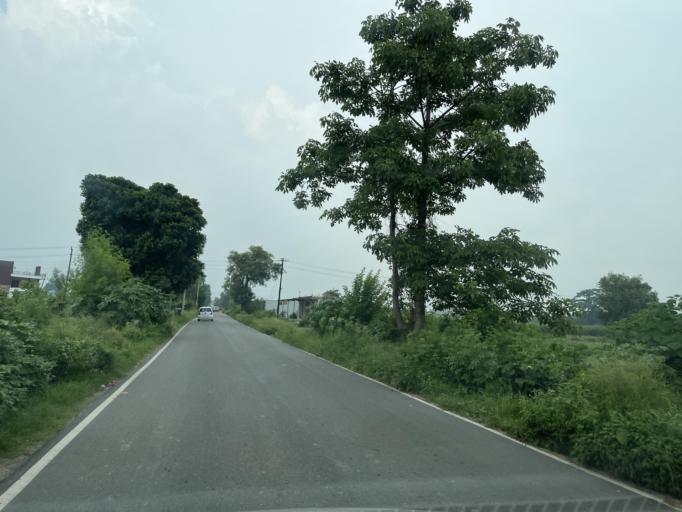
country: IN
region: Uttarakhand
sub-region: Naini Tal
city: Haldwani
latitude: 29.1799
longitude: 79.4730
